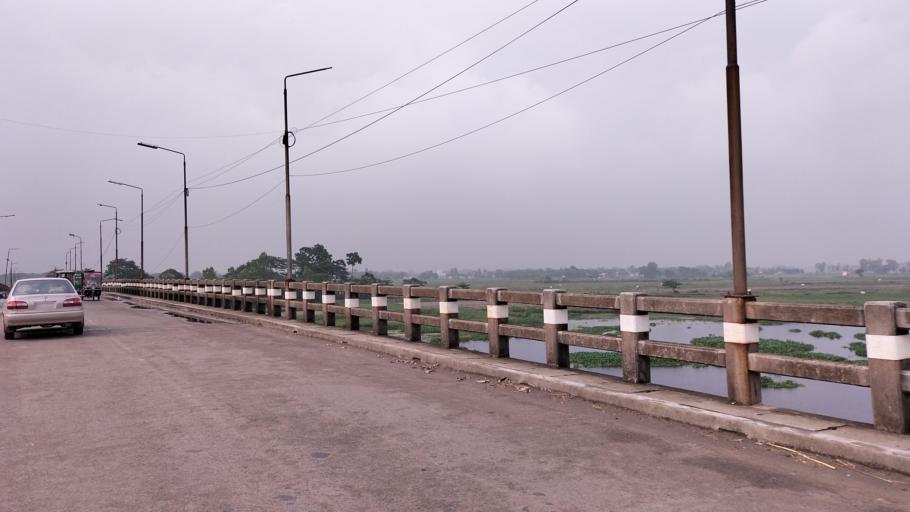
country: BD
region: Dhaka
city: Azimpur
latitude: 23.7536
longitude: 90.2497
